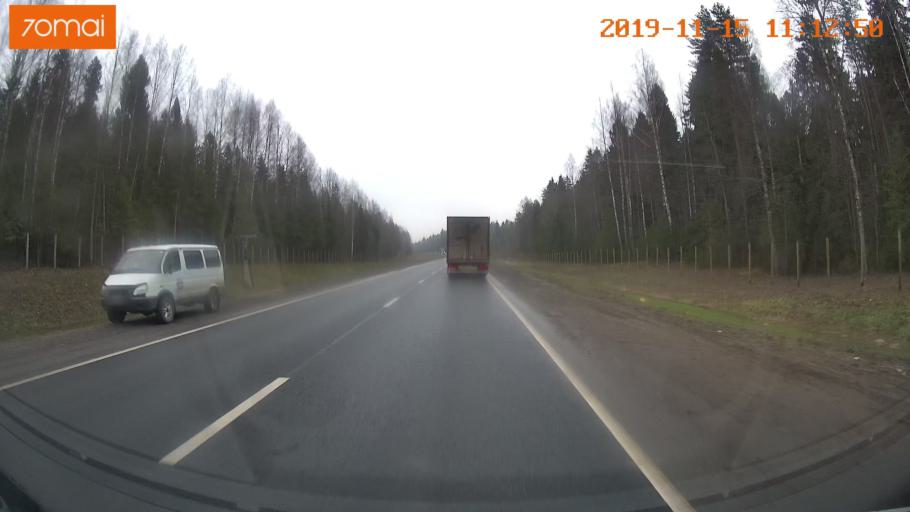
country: RU
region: Vologda
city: Chebsara
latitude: 59.1216
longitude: 39.1574
